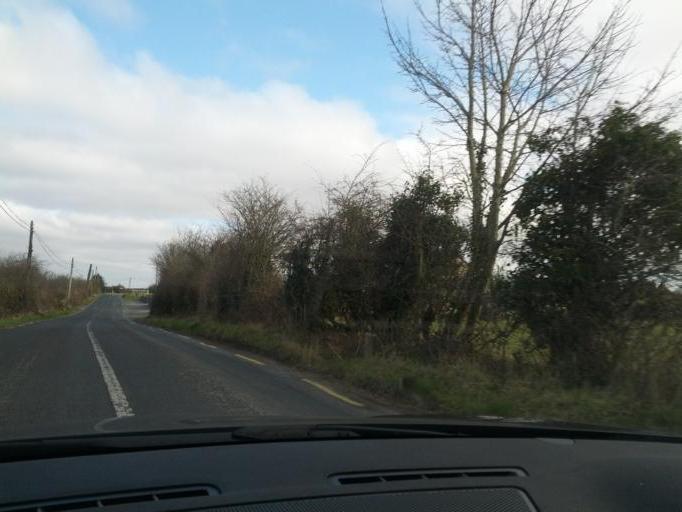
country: IE
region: Connaught
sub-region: County Galway
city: Loughrea
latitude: 53.4217
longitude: -8.5073
